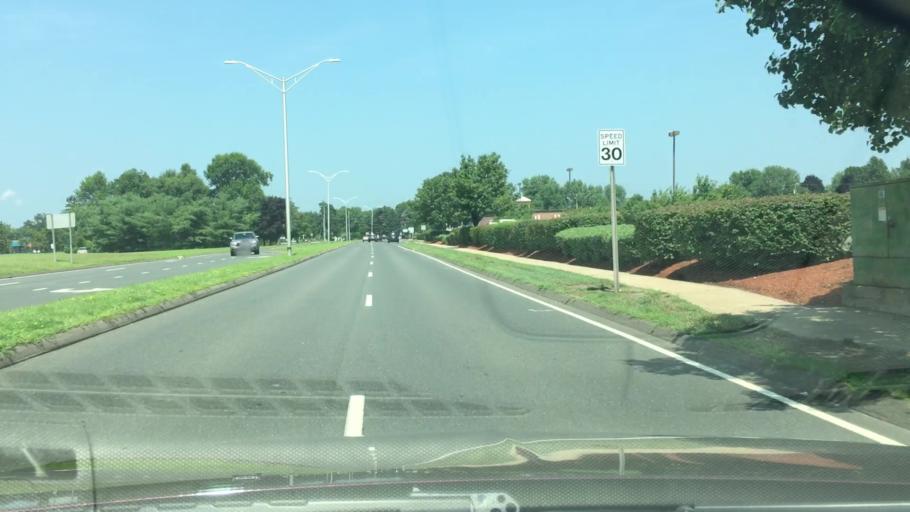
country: US
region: Connecticut
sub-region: Hartford County
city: Thompsonville
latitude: 41.9956
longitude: -72.5778
